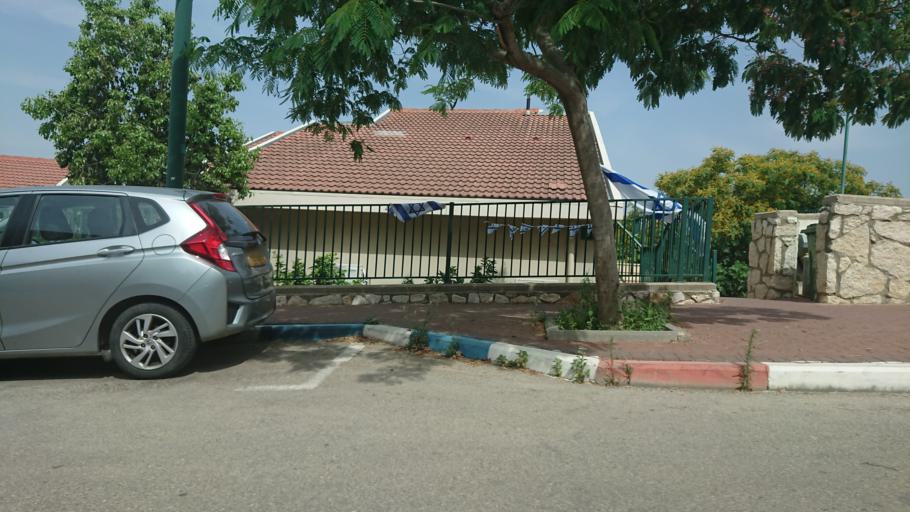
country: PS
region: West Bank
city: Rafat
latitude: 32.0641
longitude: 35.0560
